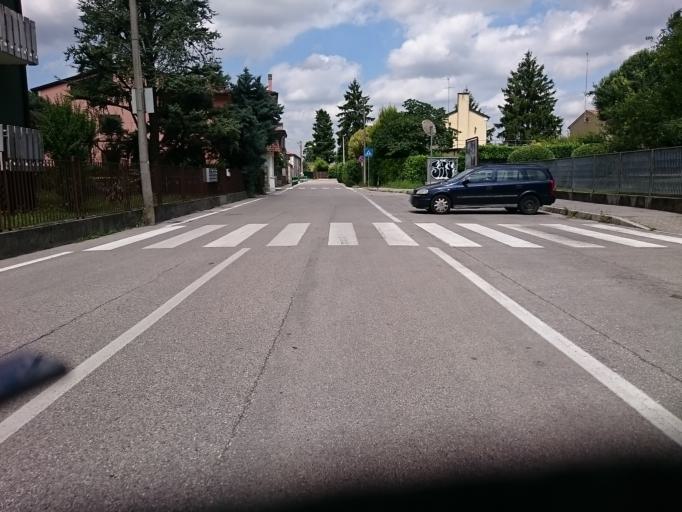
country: IT
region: Veneto
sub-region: Provincia di Padova
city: Padova
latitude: 45.3826
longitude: 11.8984
